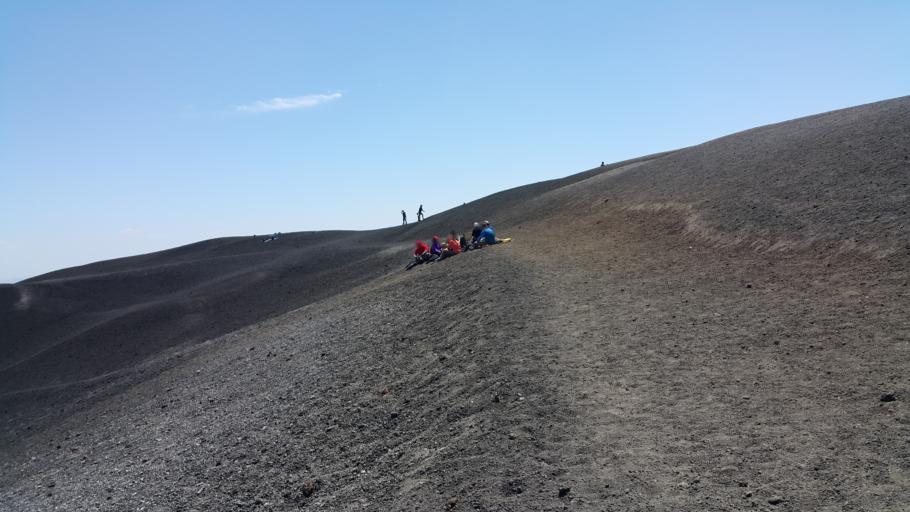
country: NI
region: Leon
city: Telica
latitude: 12.5072
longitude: -86.7042
